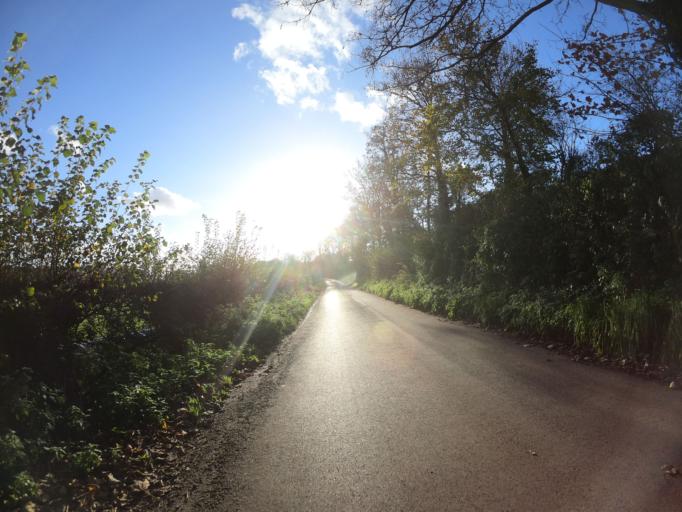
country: GB
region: England
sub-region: Kent
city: Eynsford
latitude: 51.3666
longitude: 0.1982
